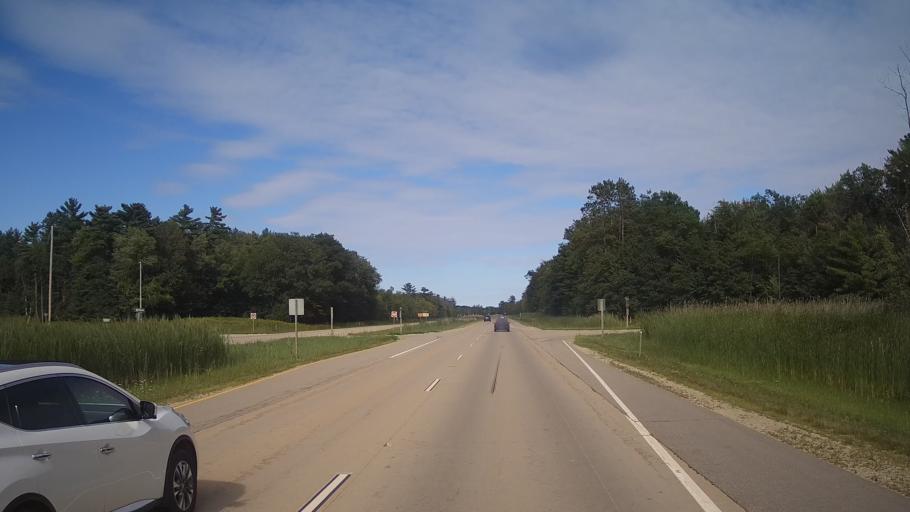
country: US
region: Wisconsin
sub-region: Oconto County
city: Oconto
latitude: 44.8114
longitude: -87.9574
